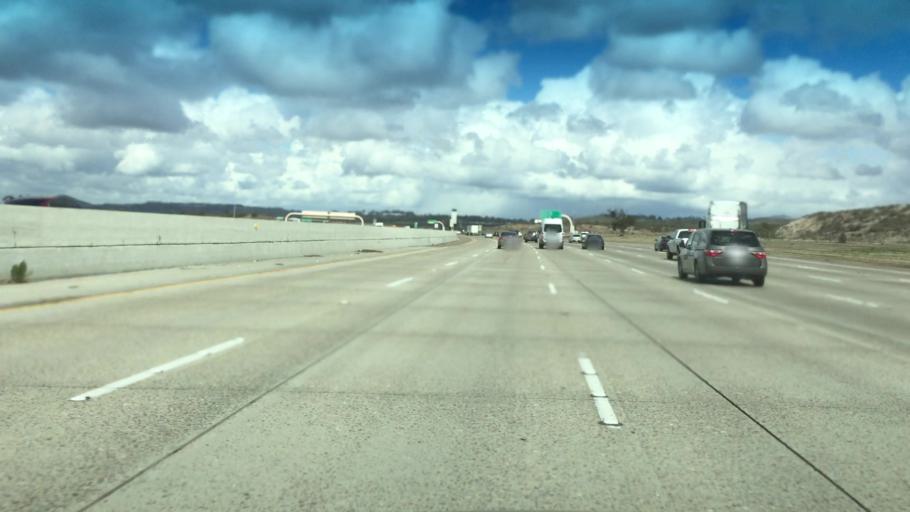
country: US
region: California
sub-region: San Diego County
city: Poway
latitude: 32.8657
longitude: -117.1090
